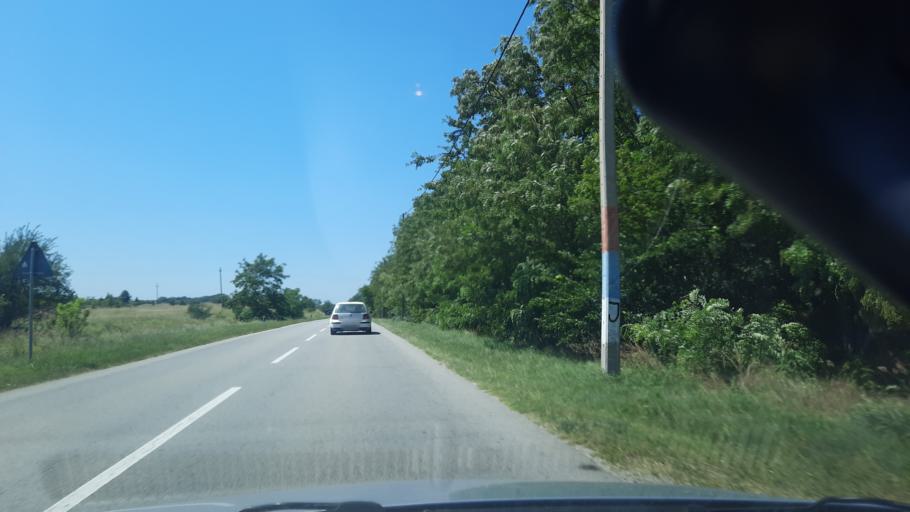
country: RS
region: Autonomna Pokrajina Vojvodina
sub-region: Juznobanatski Okrug
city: Kovin
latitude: 44.8136
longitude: 21.1564
